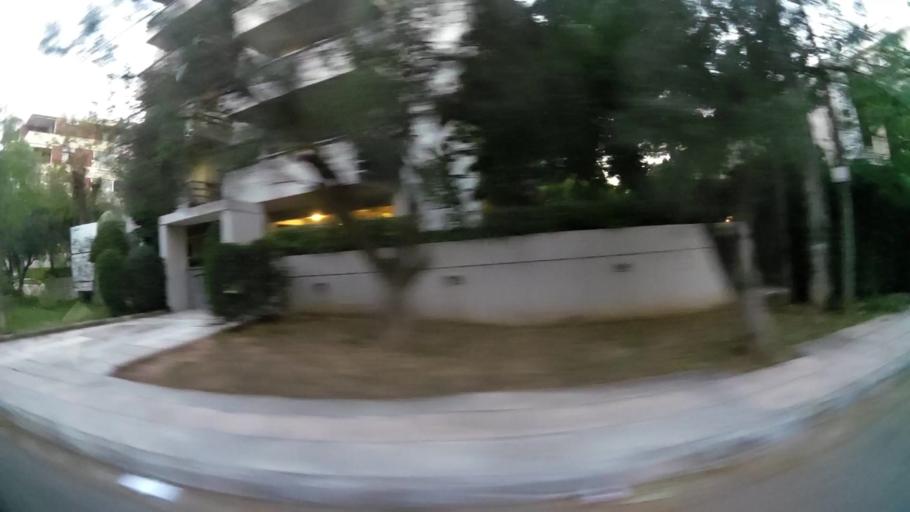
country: GR
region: Attica
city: Pefki
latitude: 38.0633
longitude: 23.8022
